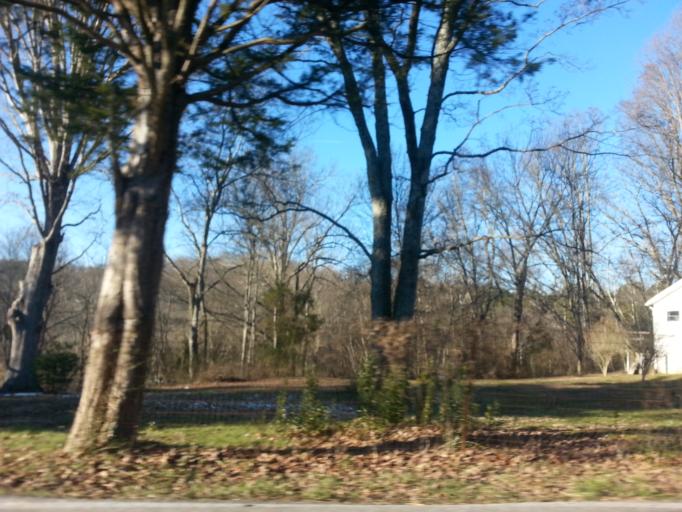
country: US
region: Tennessee
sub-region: Knox County
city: Farragut
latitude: 35.9591
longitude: -84.0620
